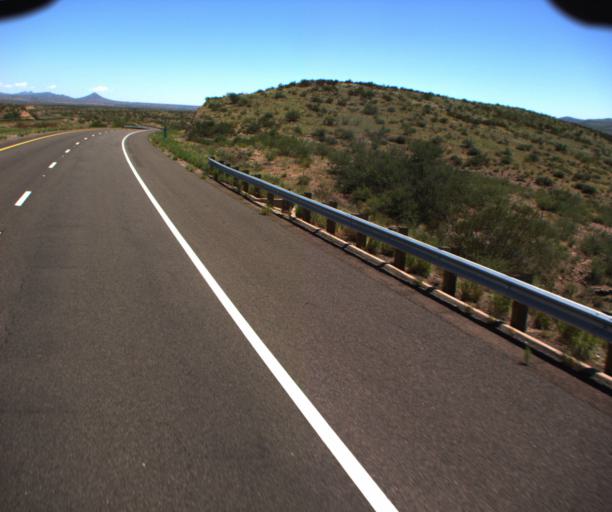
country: US
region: Arizona
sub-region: Greenlee County
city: Clifton
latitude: 32.9771
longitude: -109.2496
